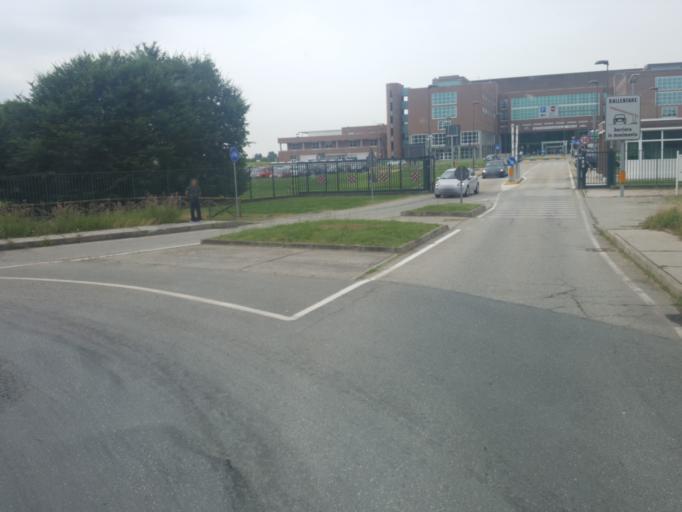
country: IT
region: Piedmont
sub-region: Provincia di Torino
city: Candiolo
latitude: 44.9682
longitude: 7.5670
